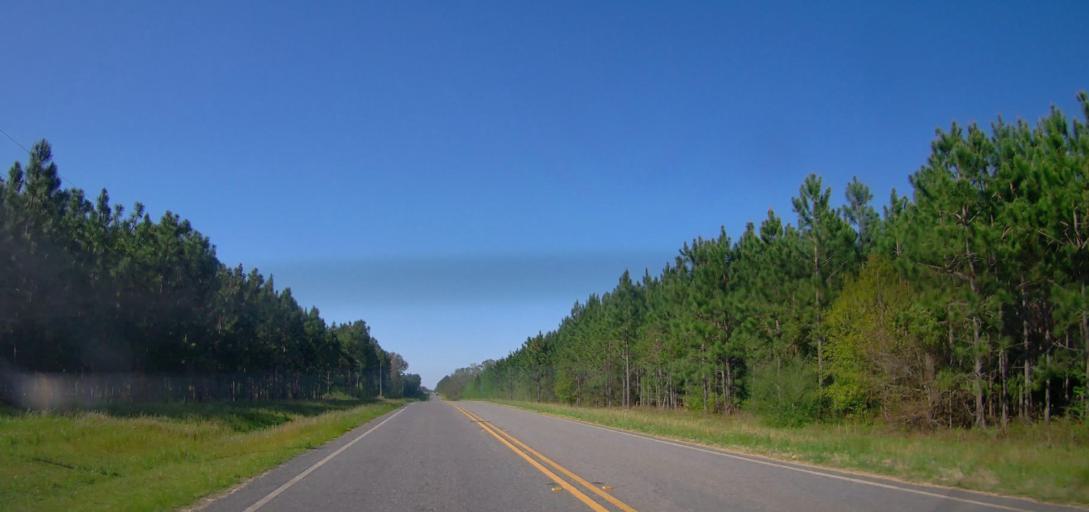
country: US
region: Georgia
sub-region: Wilcox County
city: Rochelle
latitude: 32.0438
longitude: -83.5037
